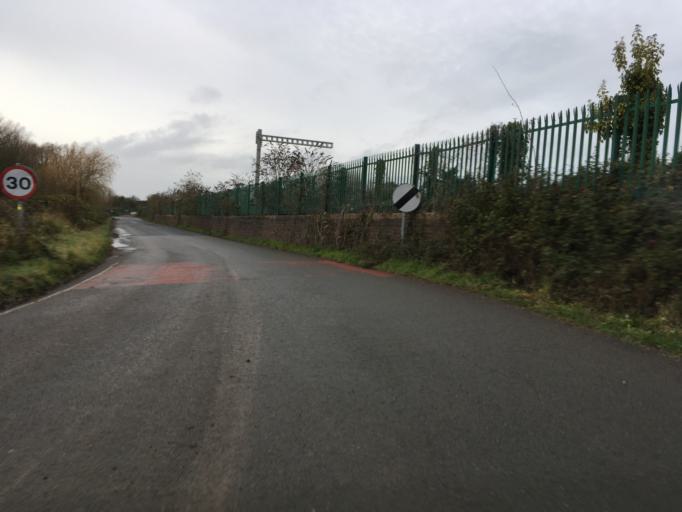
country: GB
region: Wales
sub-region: Monmouthshire
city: Magor
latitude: 51.5777
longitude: -2.8274
